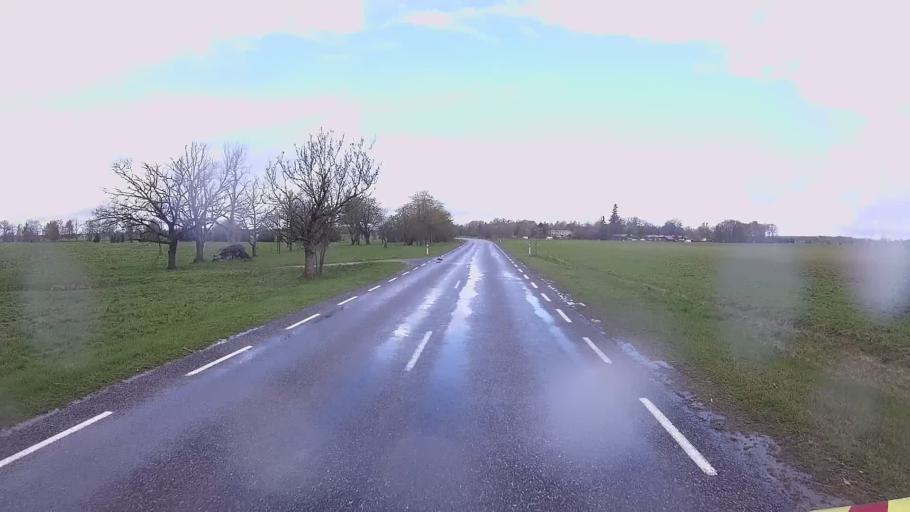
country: EE
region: Hiiumaa
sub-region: Kaerdla linn
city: Kardla
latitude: 58.8342
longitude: 22.8084
